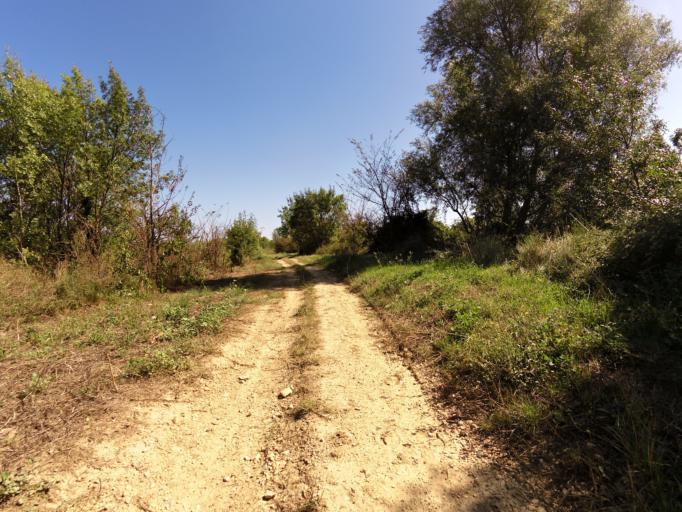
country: FR
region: Languedoc-Roussillon
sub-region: Departement du Gard
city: Codognan
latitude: 43.7370
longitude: 4.2145
